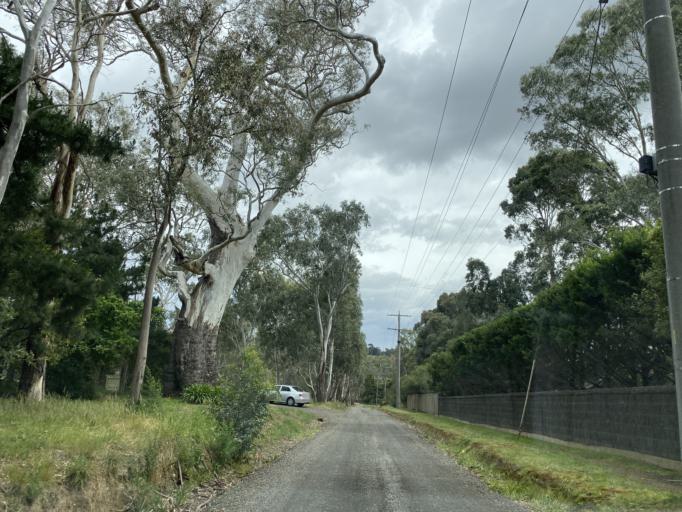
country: AU
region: Victoria
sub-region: Banyule
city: Darch
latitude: -37.7430
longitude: 145.1087
